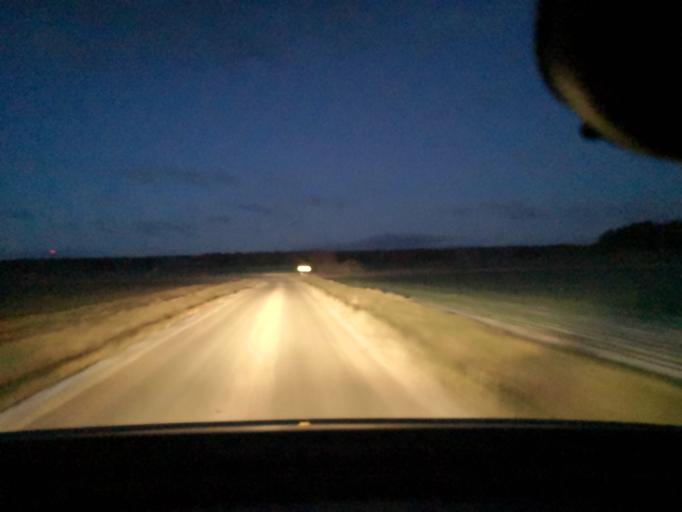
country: SE
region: Uppsala
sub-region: Heby Kommun
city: Heby
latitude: 59.9228
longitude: 16.7529
